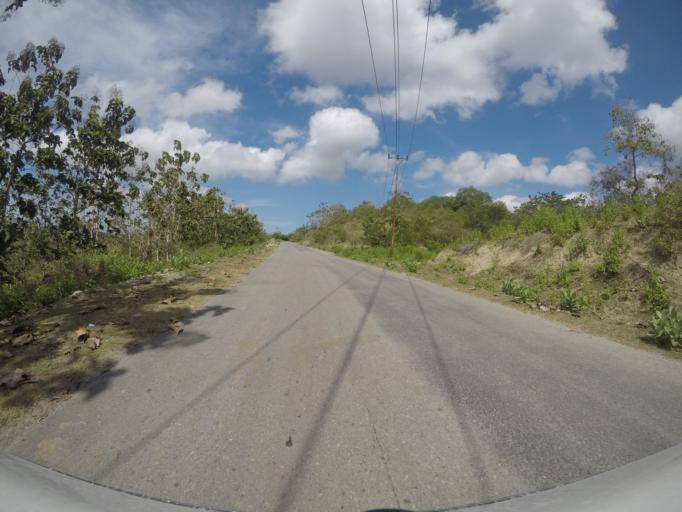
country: TL
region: Viqueque
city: Viqueque
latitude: -8.8727
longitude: 126.3600
